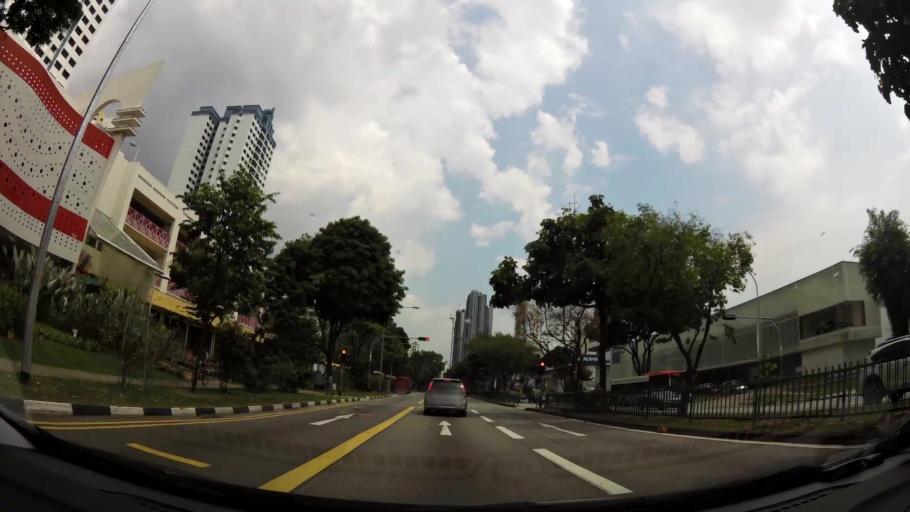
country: SG
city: Singapore
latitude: 1.2924
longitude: 103.8106
